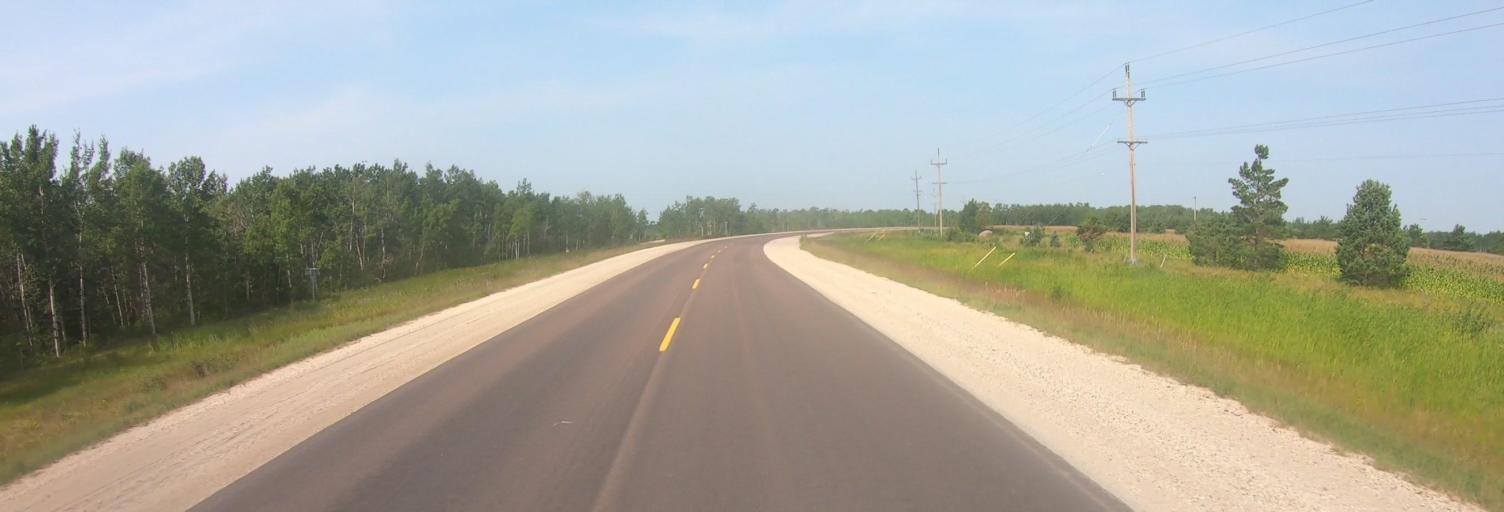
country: CA
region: Manitoba
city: La Broquerie
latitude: 49.2669
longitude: -96.4718
